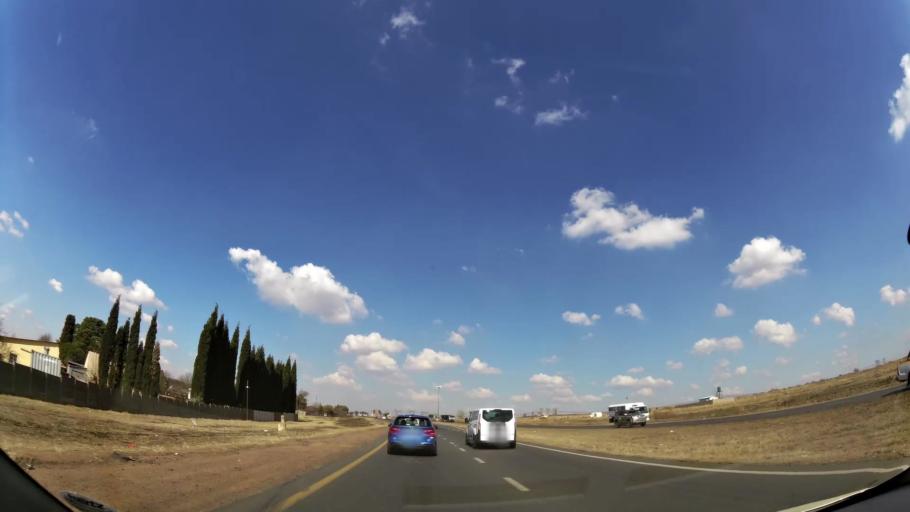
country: ZA
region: Mpumalanga
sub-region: Nkangala District Municipality
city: Witbank
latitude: -25.9331
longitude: 29.2373
